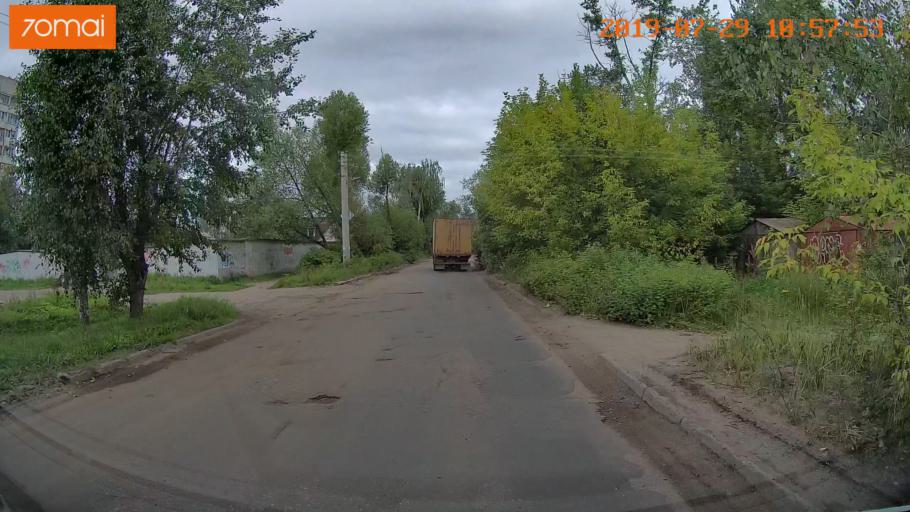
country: RU
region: Ivanovo
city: Bogorodskoye
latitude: 56.9912
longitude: 41.0378
